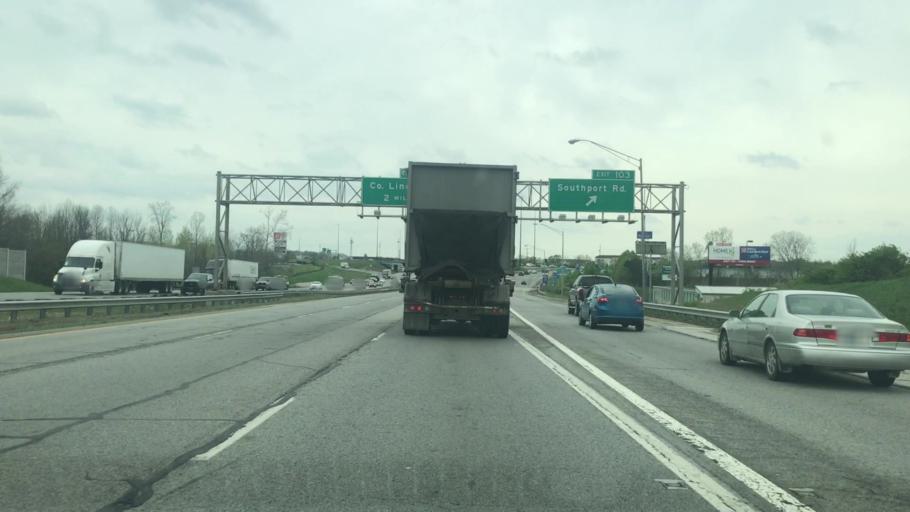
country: US
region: Indiana
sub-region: Marion County
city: Southport
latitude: 39.6693
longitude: -86.0952
